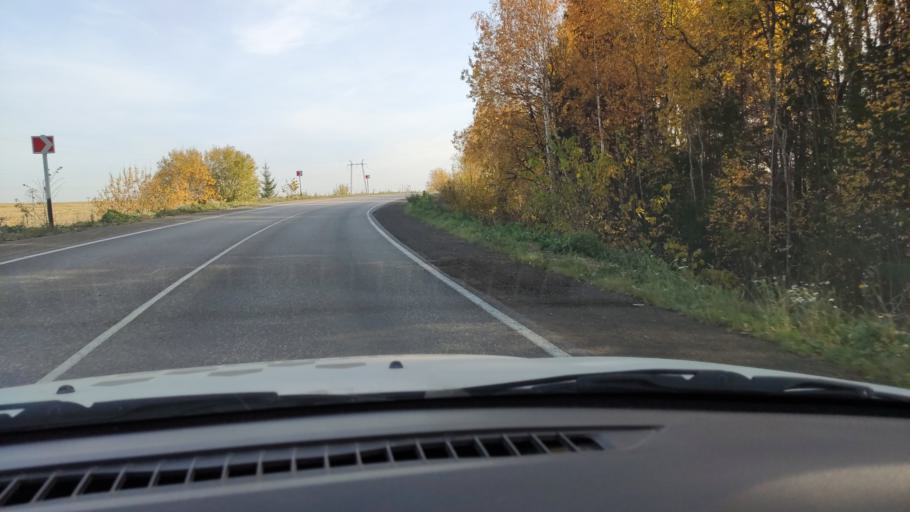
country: RU
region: Perm
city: Novyye Lyady
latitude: 58.0300
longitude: 56.6884
